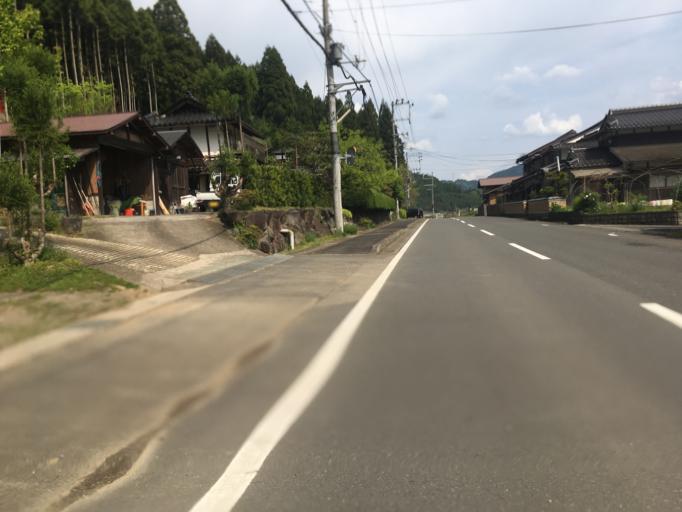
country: JP
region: Kyoto
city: Kameoka
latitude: 35.1448
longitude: 135.5812
